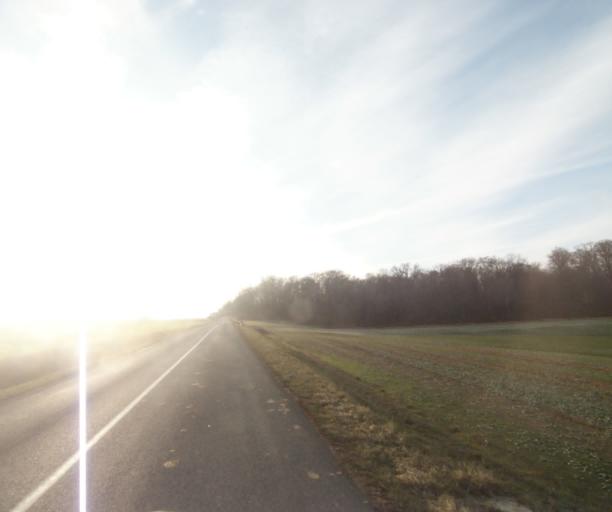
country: FR
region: Champagne-Ardenne
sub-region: Departement de la Haute-Marne
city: Chancenay
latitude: 48.7200
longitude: 4.9428
